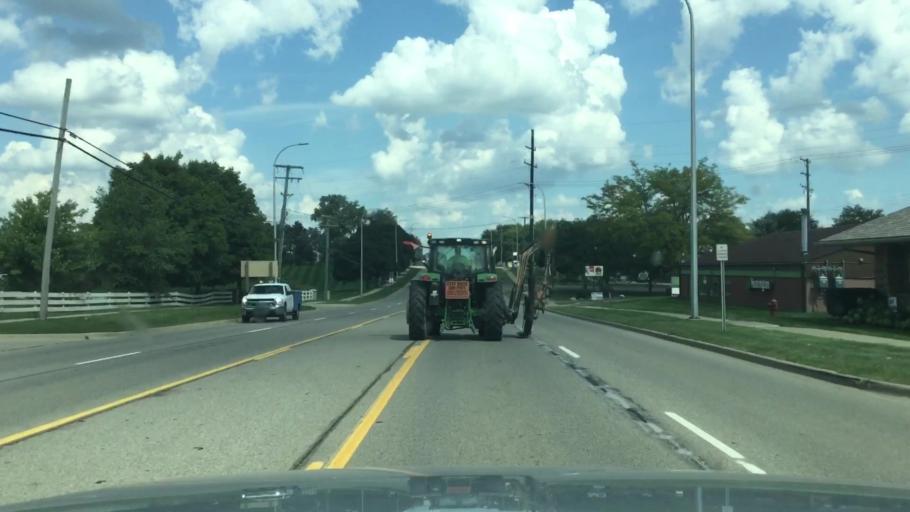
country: US
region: Michigan
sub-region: Washtenaw County
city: Saline
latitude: 42.1706
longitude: -83.7729
